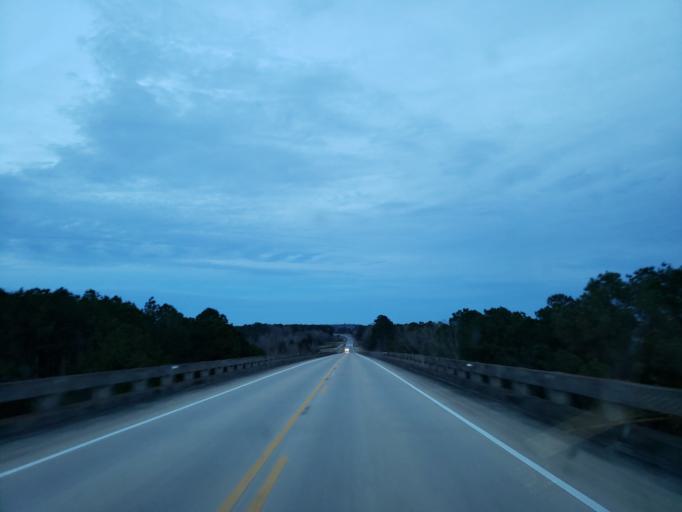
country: US
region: Alabama
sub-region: Greene County
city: Eutaw
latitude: 32.8398
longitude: -88.1364
